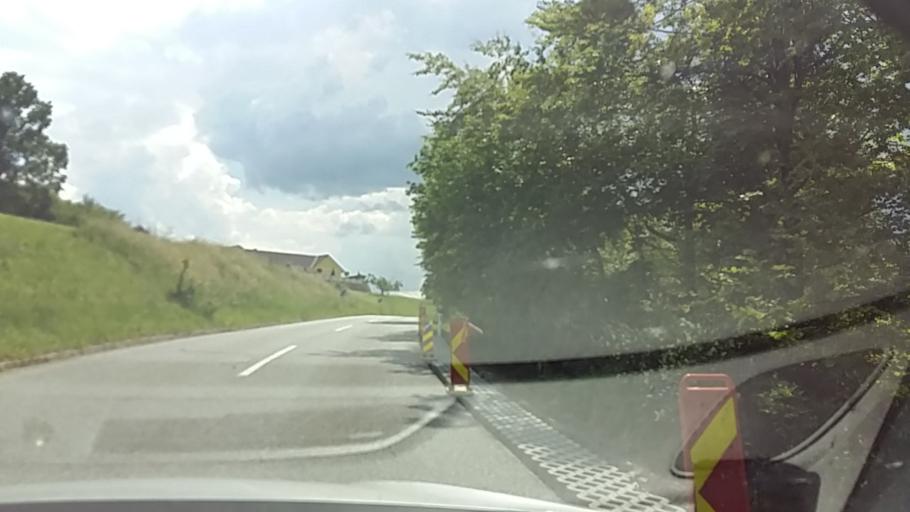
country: AT
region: Styria
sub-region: Politischer Bezirk Suedoststeiermark
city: Breitenfeld an der Rittschein
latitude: 47.0247
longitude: 15.9505
